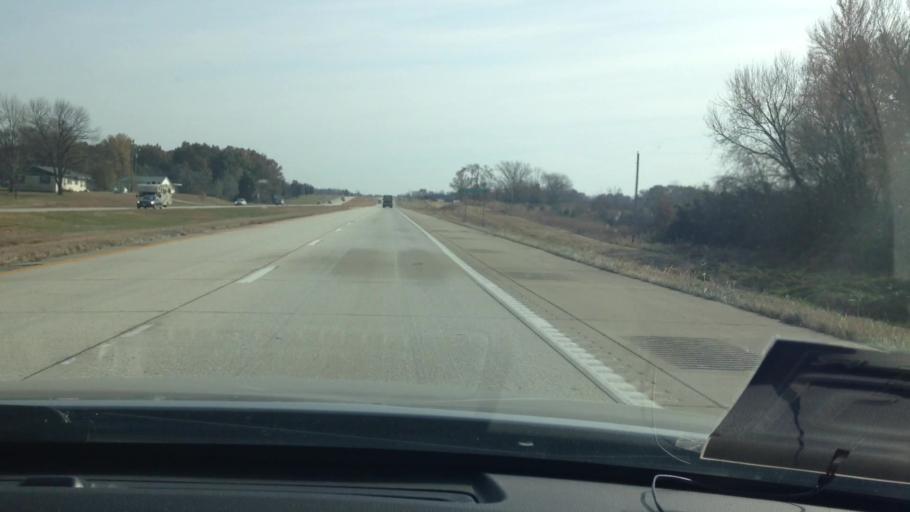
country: US
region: Missouri
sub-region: Henry County
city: Clinton
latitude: 38.4189
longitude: -93.8670
